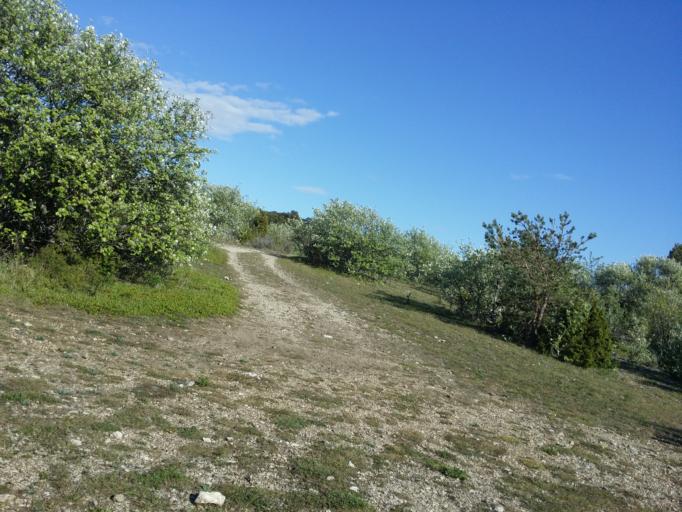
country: SE
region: Gotland
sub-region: Gotland
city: Vibble
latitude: 57.6194
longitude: 18.2635
